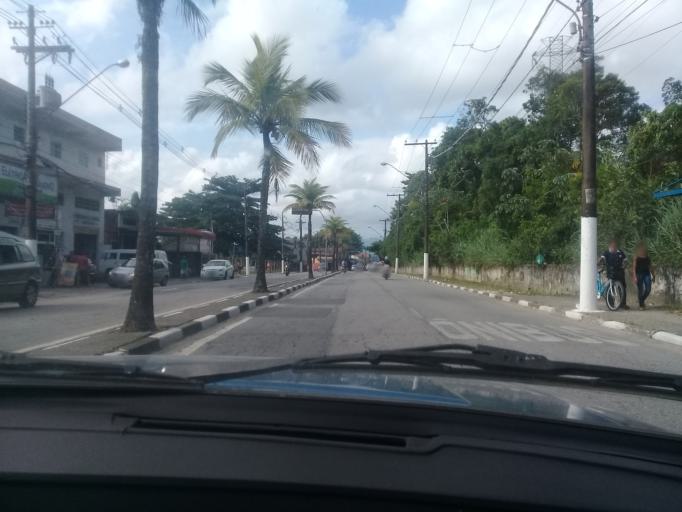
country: BR
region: Sao Paulo
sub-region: Guaruja
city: Guaruja
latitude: -23.9987
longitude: -46.2741
